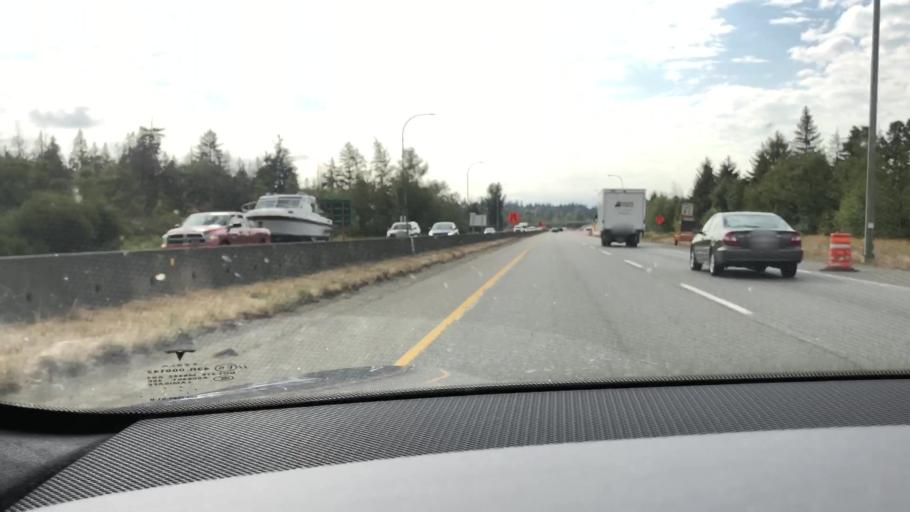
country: CA
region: British Columbia
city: Delta
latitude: 49.1395
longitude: -122.9339
